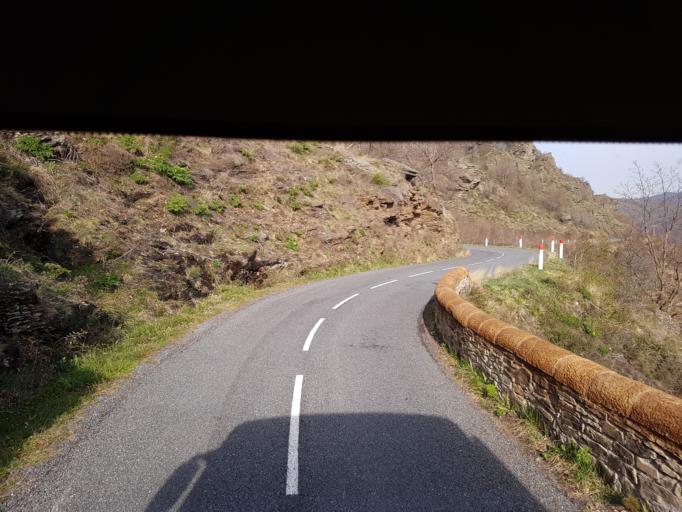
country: FR
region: Languedoc-Roussillon
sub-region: Departement du Gard
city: Branoux-les-Taillades
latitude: 44.3278
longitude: 3.8446
